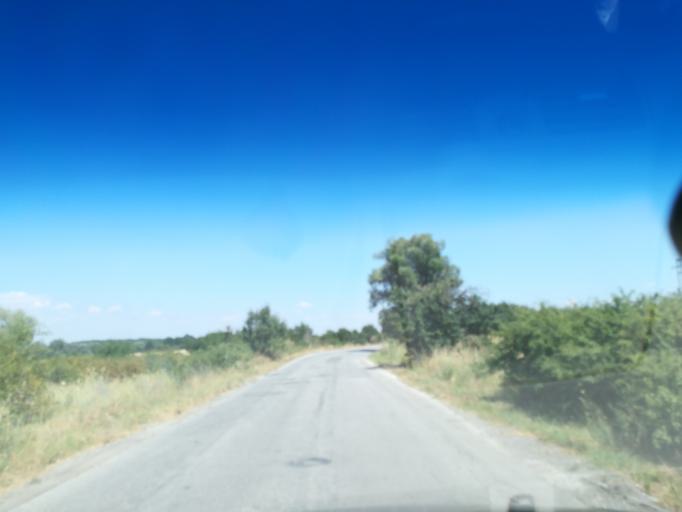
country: BG
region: Plovdiv
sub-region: Obshtina Sadovo
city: Sadovo
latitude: 42.0232
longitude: 25.0132
